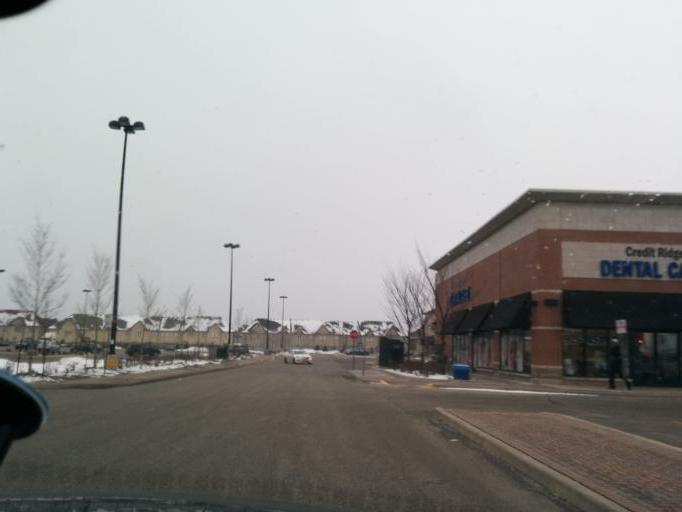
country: CA
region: Ontario
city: Brampton
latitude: 43.6571
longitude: -79.8143
